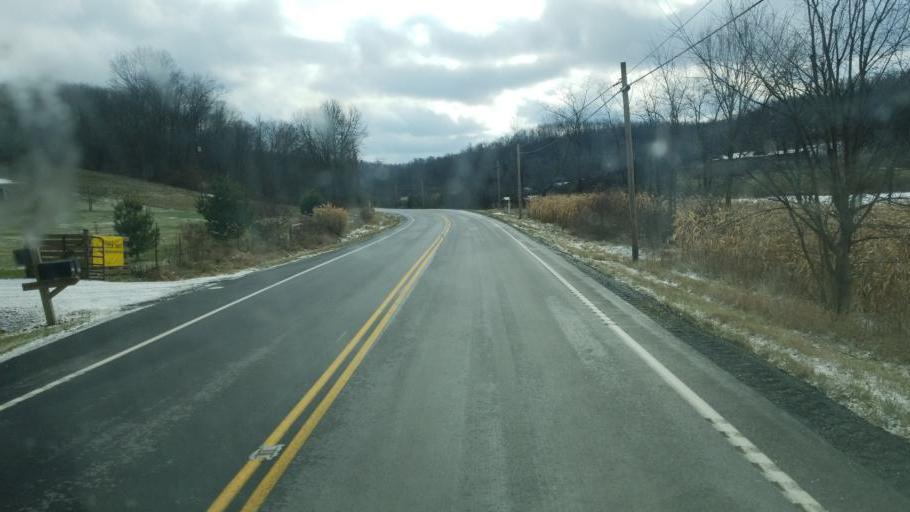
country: US
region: Ohio
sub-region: Muskingum County
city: Frazeysburg
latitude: 40.1269
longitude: -82.1944
